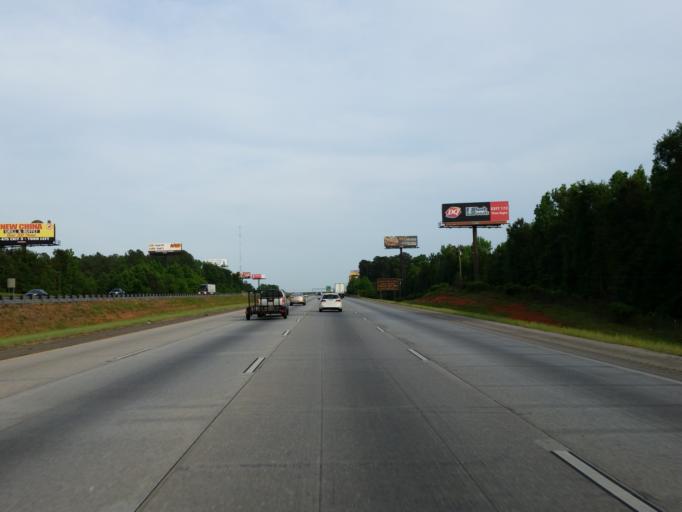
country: US
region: Georgia
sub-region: Monroe County
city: Forsyth
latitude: 32.9688
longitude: -83.8238
